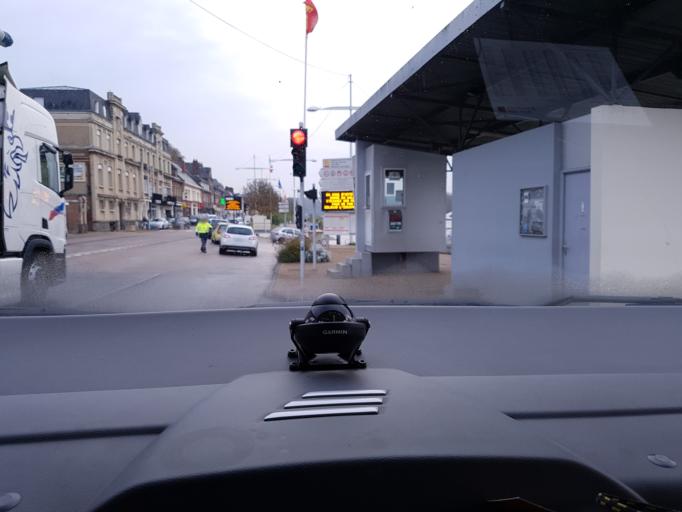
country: FR
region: Haute-Normandie
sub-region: Departement de la Seine-Maritime
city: Duclair
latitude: 49.4807
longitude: 0.8747
